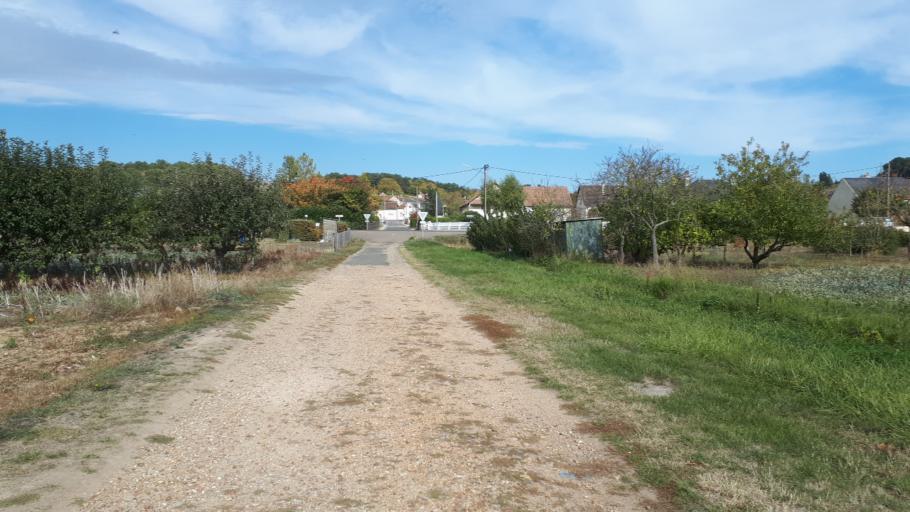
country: FR
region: Centre
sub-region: Departement du Loir-et-Cher
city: Villiers-sur-Loir
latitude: 47.8014
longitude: 0.9961
